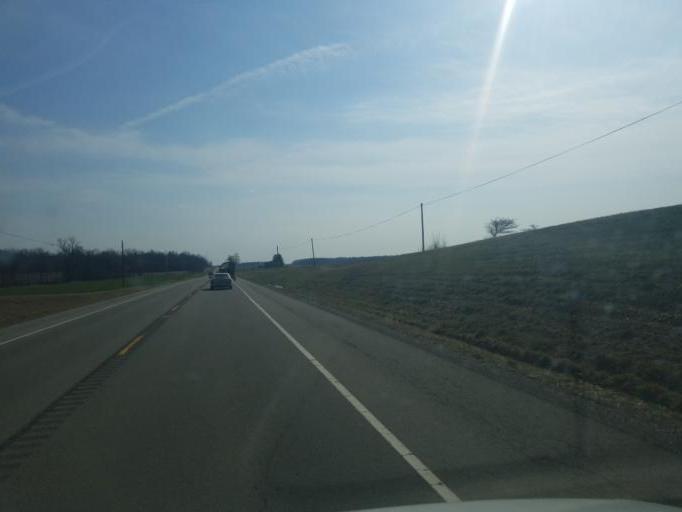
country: US
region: Ohio
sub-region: Logan County
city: Northwood
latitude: 40.5388
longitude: -83.6746
